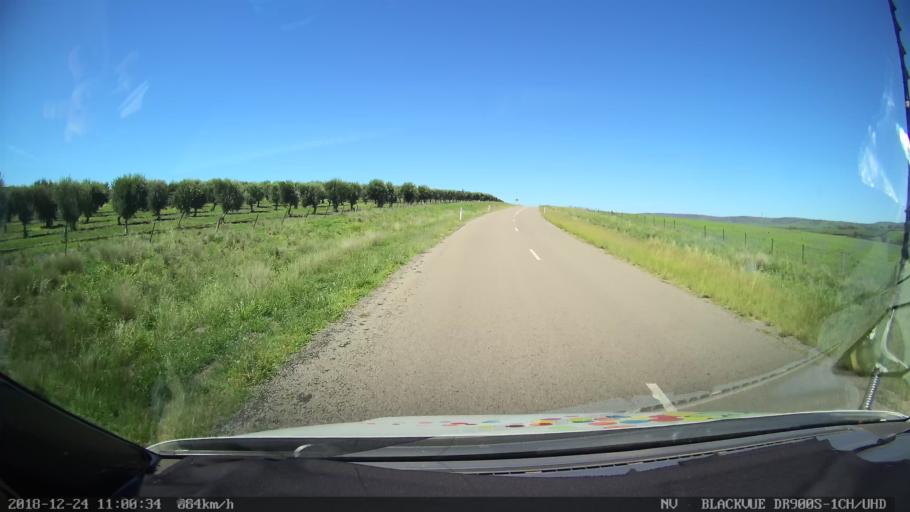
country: AU
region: New South Wales
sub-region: Upper Hunter Shire
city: Merriwa
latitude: -32.0692
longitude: 150.3932
